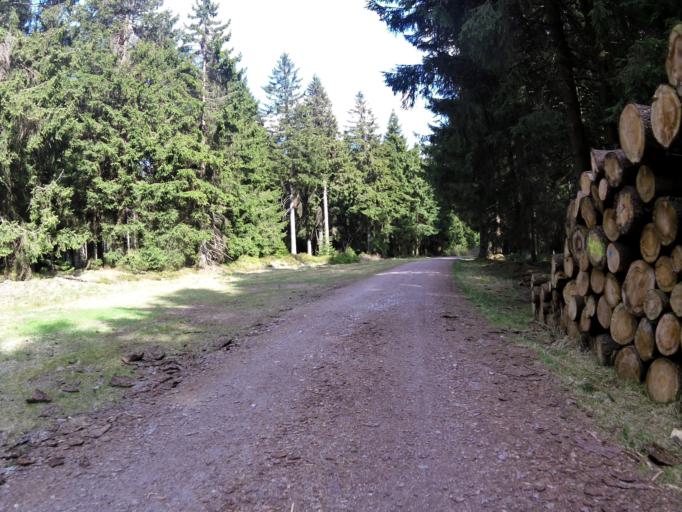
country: DE
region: Thuringia
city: Oberhof
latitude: 50.7000
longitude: 10.7089
